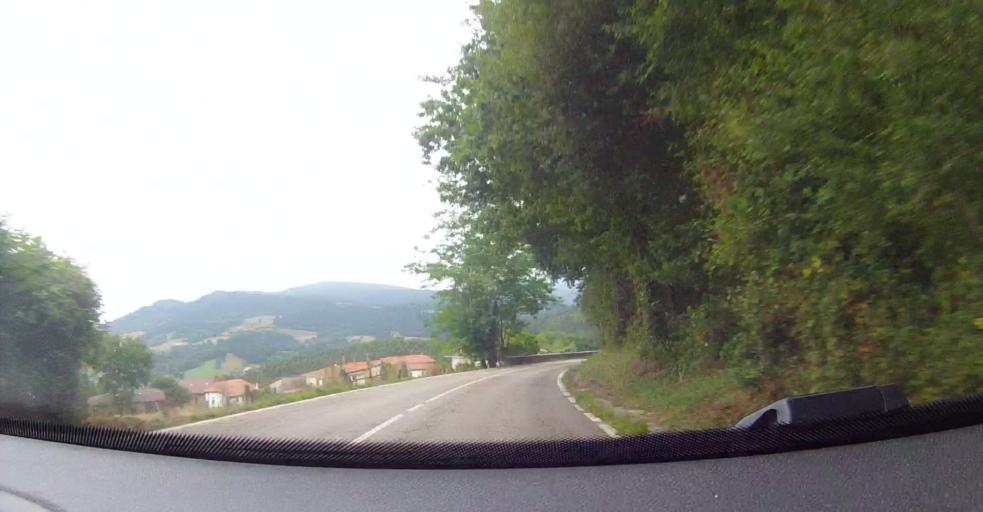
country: ES
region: Basque Country
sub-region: Bizkaia
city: Balmaseda
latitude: 43.2481
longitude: -3.2751
